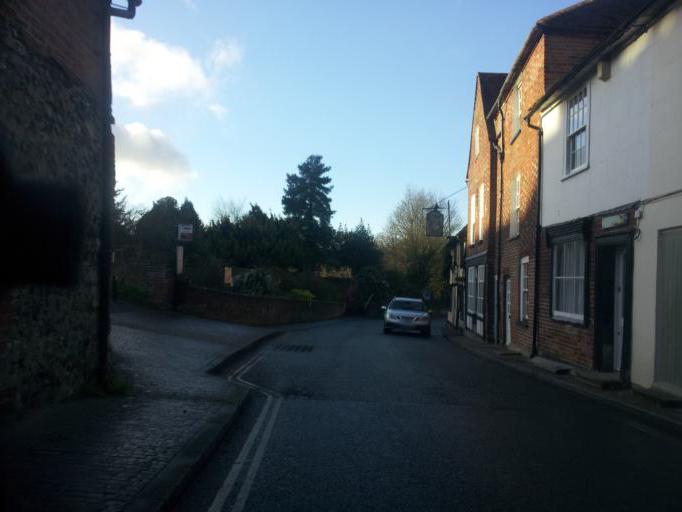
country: GB
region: England
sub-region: Kent
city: Meopham
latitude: 51.3904
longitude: 0.3991
